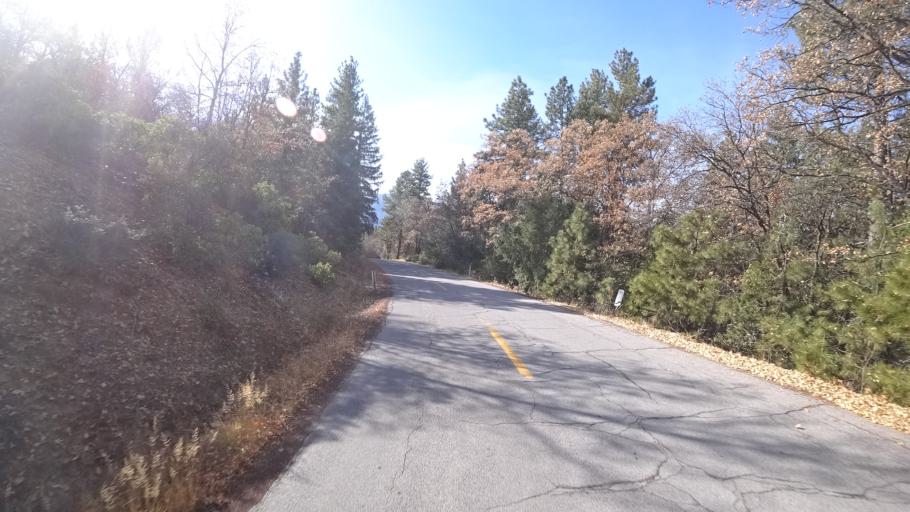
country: US
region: California
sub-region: Siskiyou County
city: Weed
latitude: 41.4319
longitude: -122.4166
